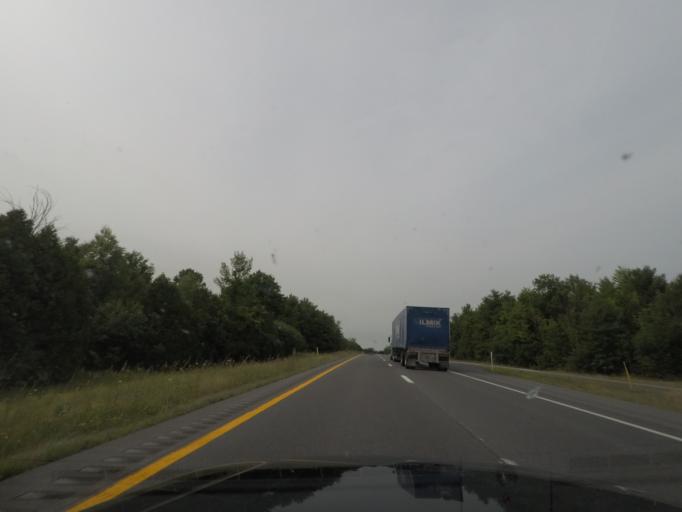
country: US
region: New York
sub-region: Clinton County
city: Cumberland Head
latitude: 44.8077
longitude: -73.4447
